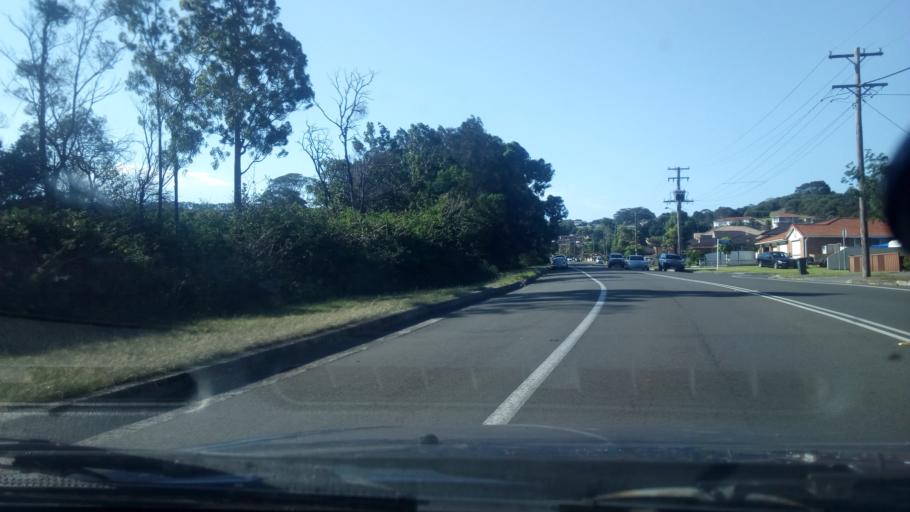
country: AU
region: New South Wales
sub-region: Wollongong
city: Berkeley
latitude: -34.4783
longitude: 150.8553
